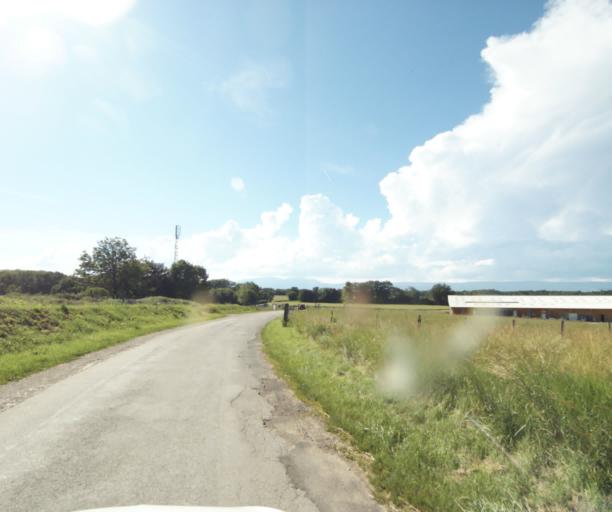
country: FR
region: Rhone-Alpes
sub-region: Departement de la Haute-Savoie
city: Massongy
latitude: 46.3248
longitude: 6.3177
